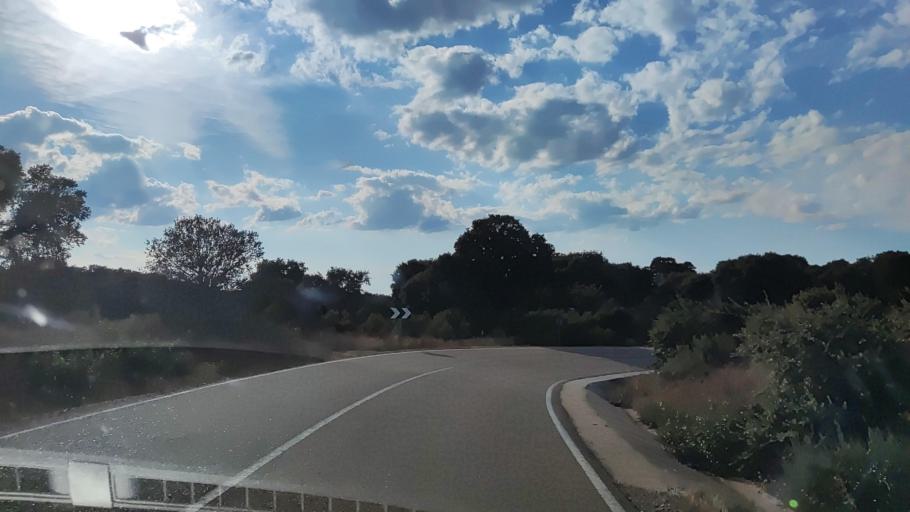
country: ES
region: Castille and Leon
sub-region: Provincia de Salamanca
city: Pastores
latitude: 40.5221
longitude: -6.5190
